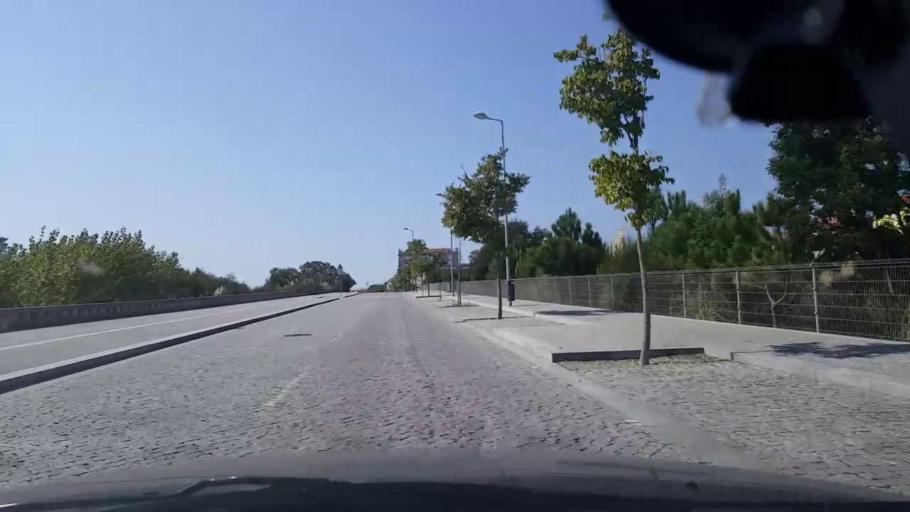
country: PT
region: Porto
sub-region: Vila do Conde
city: Vila do Conde
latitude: 41.3523
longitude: -8.7321
